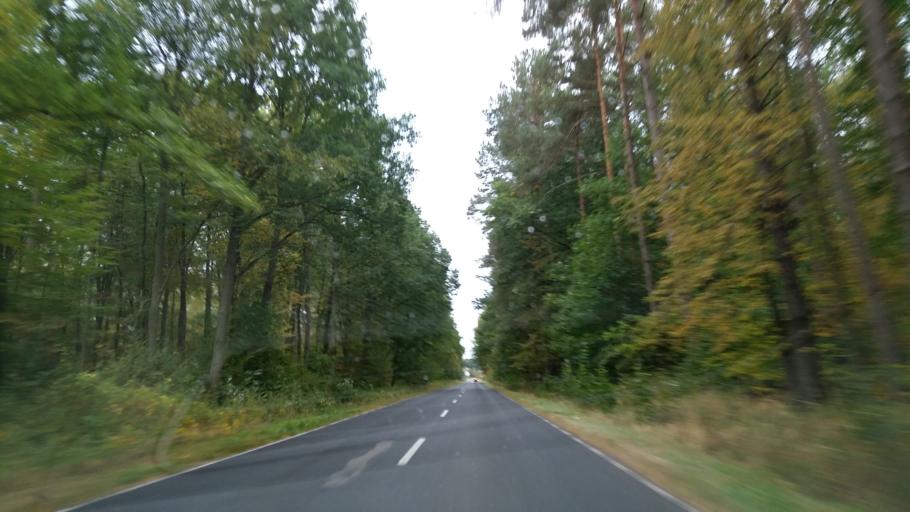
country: PL
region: Lubusz
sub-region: Powiat gorzowski
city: Klodawa
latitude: 52.8905
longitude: 15.1920
